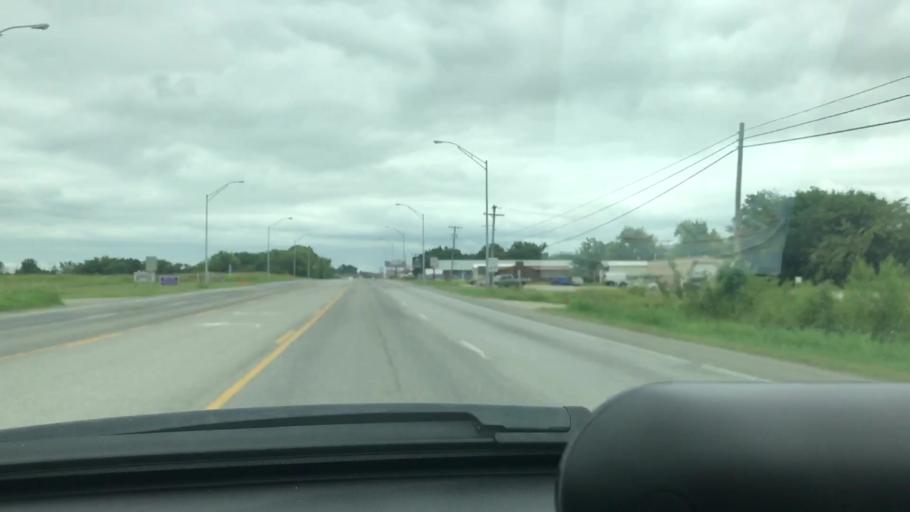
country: US
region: Oklahoma
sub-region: Wagoner County
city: Wagoner
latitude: 35.9504
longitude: -95.3952
